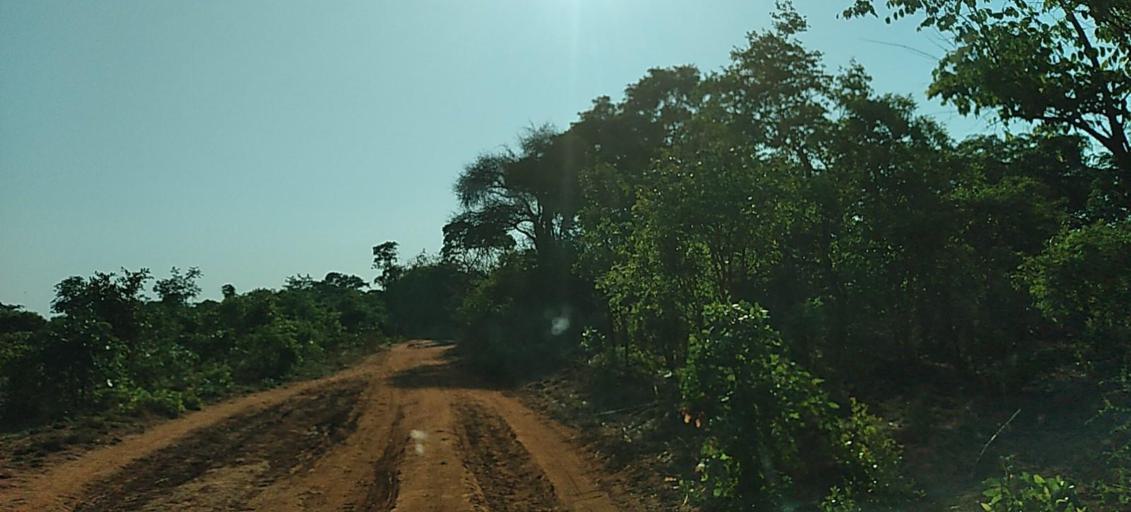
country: ZM
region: Copperbelt
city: Luanshya
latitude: -13.4591
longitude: 28.8197
